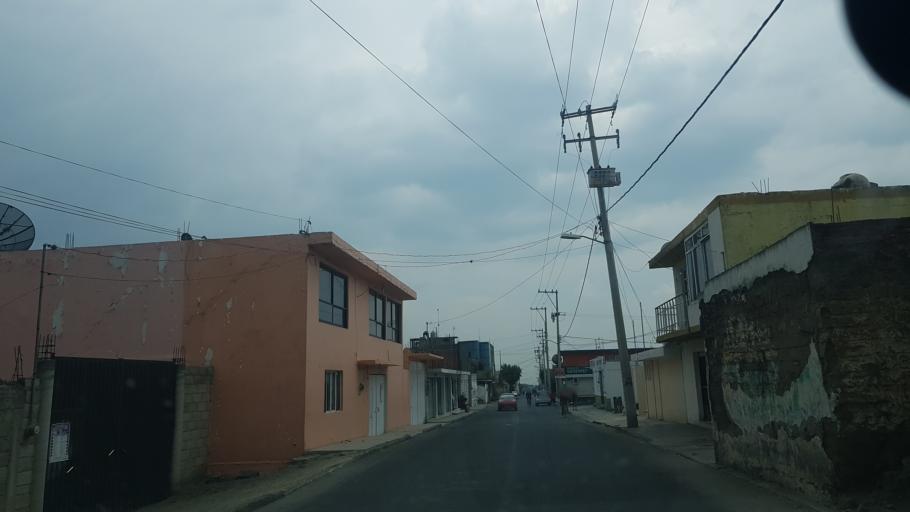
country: MX
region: Puebla
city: San Lorenzo Chiautzingo
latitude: 19.2000
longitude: -98.4595
